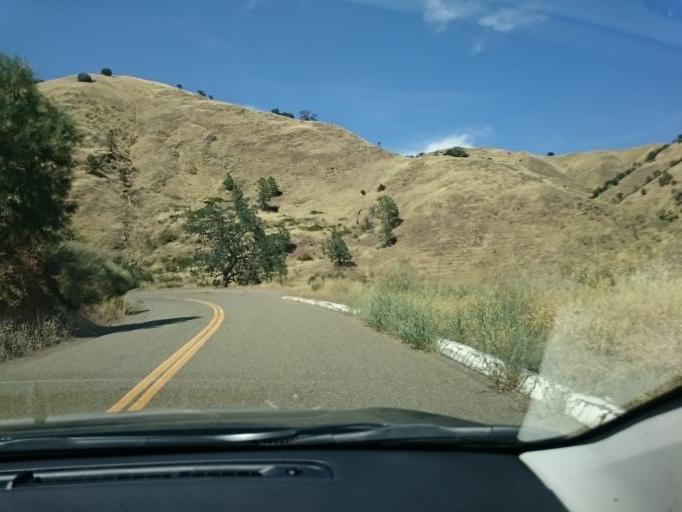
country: US
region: California
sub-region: Stanislaus County
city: Patterson
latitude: 37.4387
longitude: -121.3329
